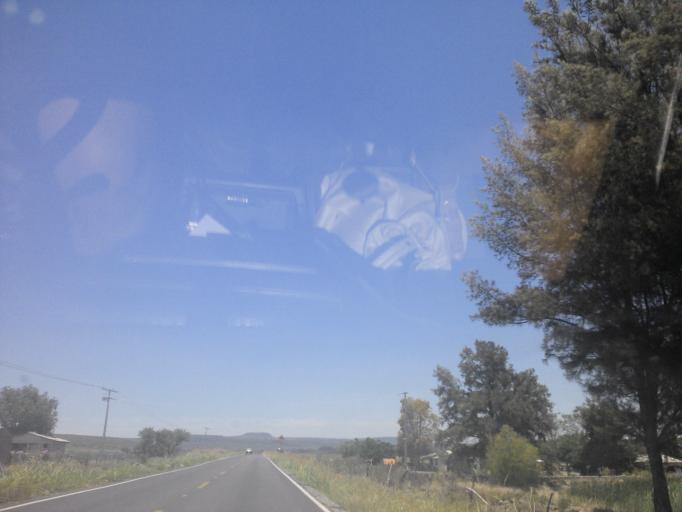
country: MX
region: Guanajuato
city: Ciudad Manuel Doblado
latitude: 20.8530
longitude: -101.9995
